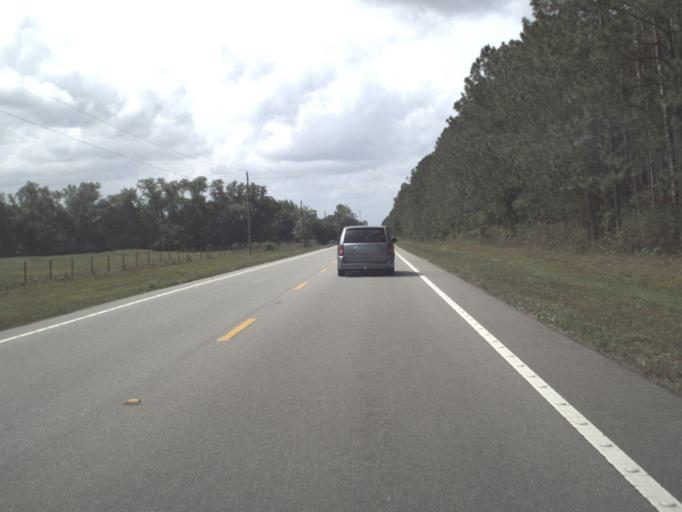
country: US
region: Florida
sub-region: Putnam County
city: Crescent City
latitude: 29.5184
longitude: -81.5042
